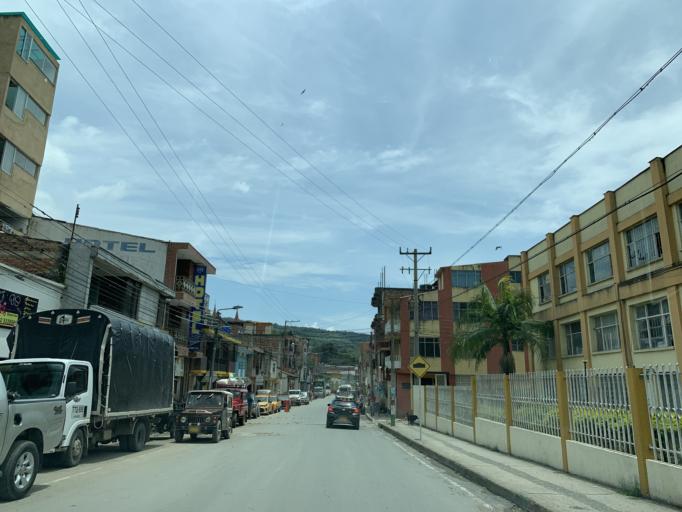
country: CO
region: Boyaca
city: Moniquira
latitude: 5.8773
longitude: -73.5687
